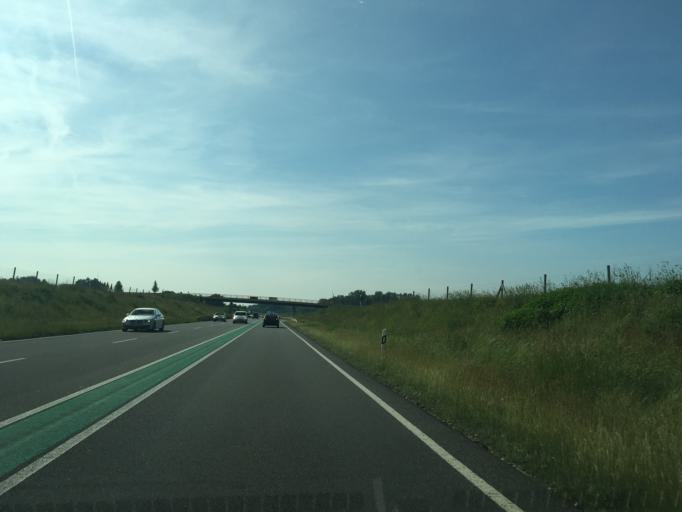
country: DE
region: North Rhine-Westphalia
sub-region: Regierungsbezirk Munster
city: Steinfurt
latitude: 52.1668
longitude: 7.3021
